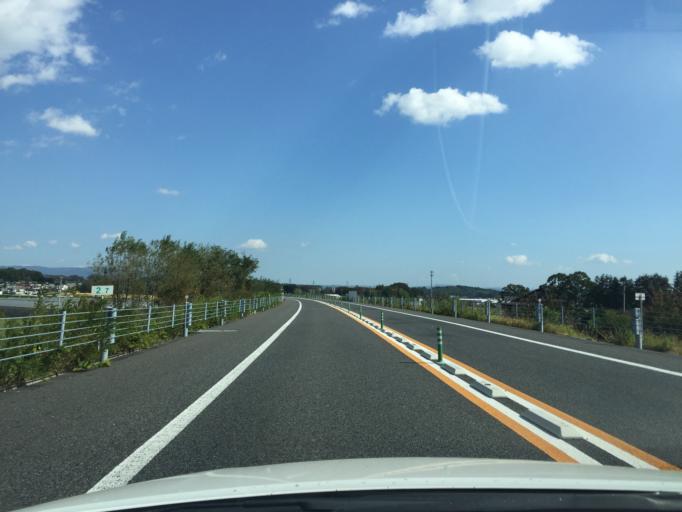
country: JP
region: Fukushima
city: Sukagawa
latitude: 37.1881
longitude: 140.3240
